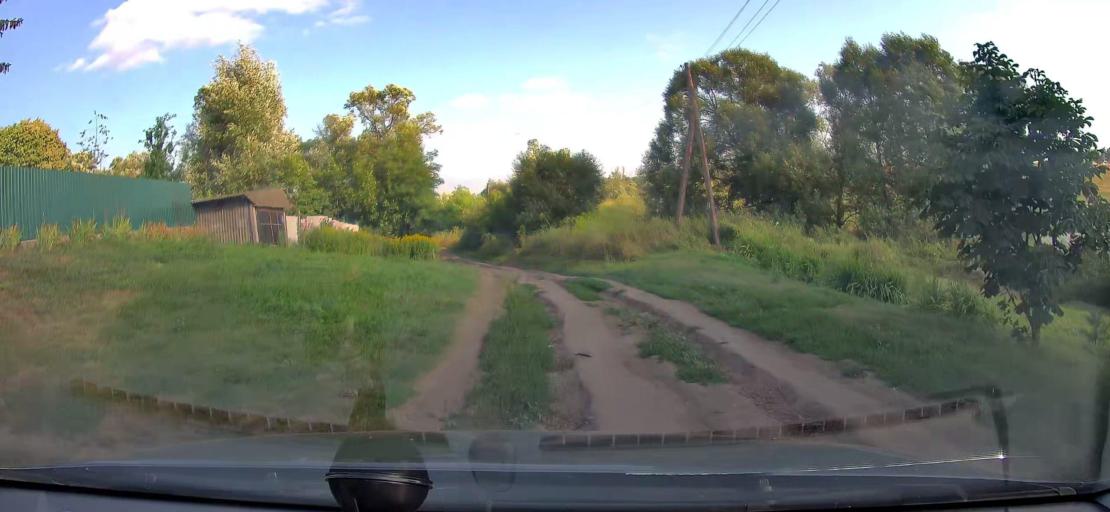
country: RU
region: Kursk
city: Zolotukhino
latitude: 52.0275
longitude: 36.2020
